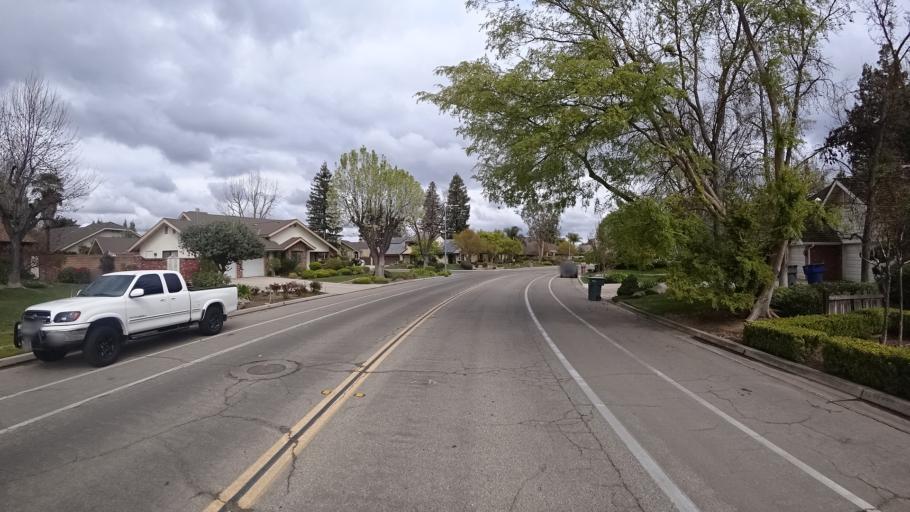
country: US
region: California
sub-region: Fresno County
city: Fresno
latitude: 36.8481
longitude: -119.8454
